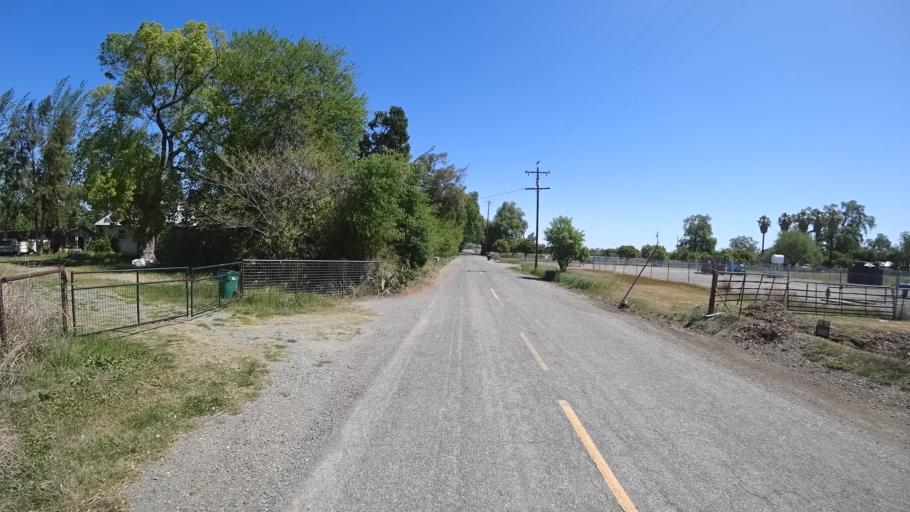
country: US
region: California
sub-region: Glenn County
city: Orland
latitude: 39.7953
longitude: -122.2451
